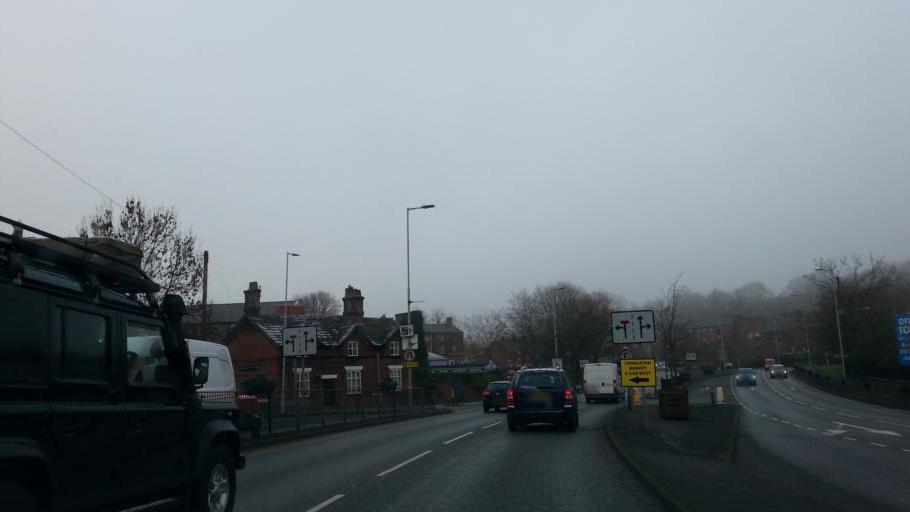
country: GB
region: England
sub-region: Cheshire East
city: Congleton
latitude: 53.1649
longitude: -2.2118
